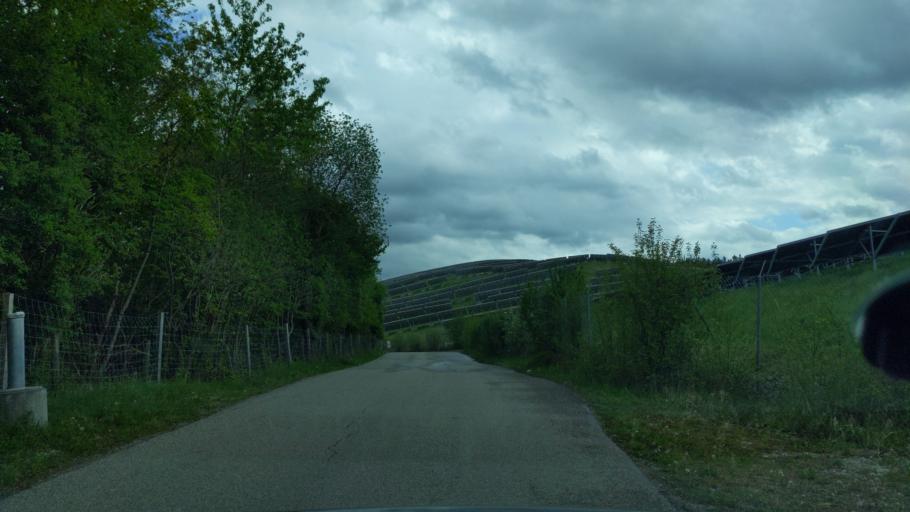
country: DE
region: Bavaria
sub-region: Upper Bavaria
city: Ebersberg
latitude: 48.1120
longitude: 11.9829
